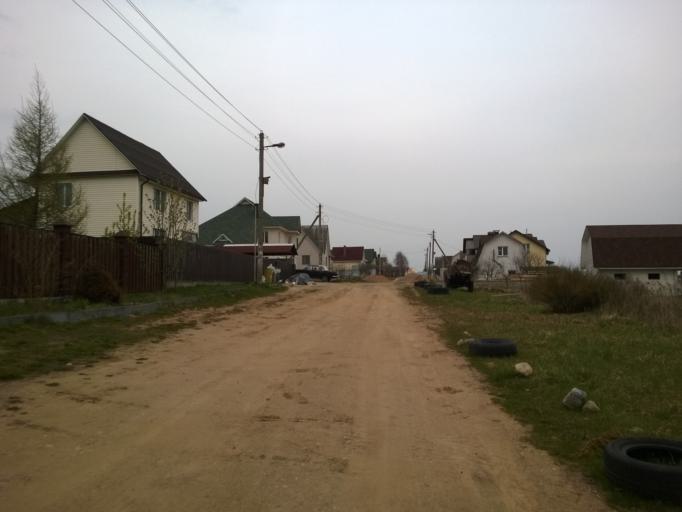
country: BY
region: Minsk
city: Slabada
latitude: 54.0050
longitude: 27.8552
